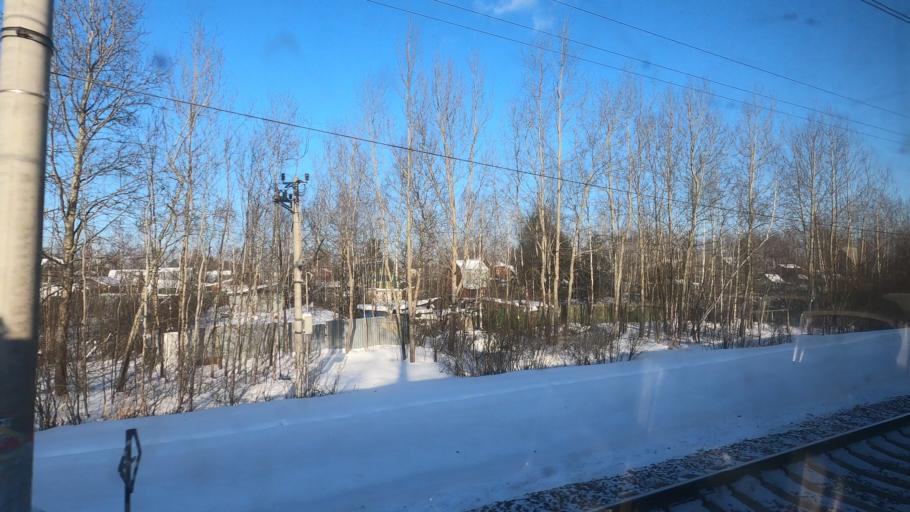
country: RU
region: Moskovskaya
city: Imeni Vorovskogo
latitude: 55.7224
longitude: 38.2830
